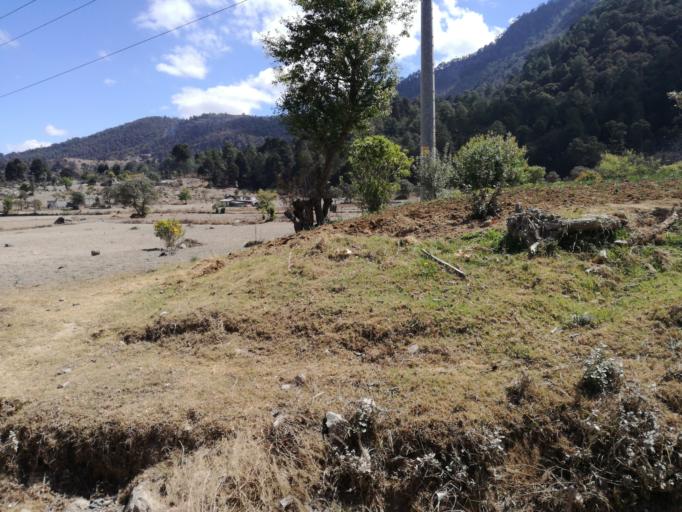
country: GT
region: Quetzaltenango
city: Quetzaltenango
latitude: 14.7972
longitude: -91.5375
